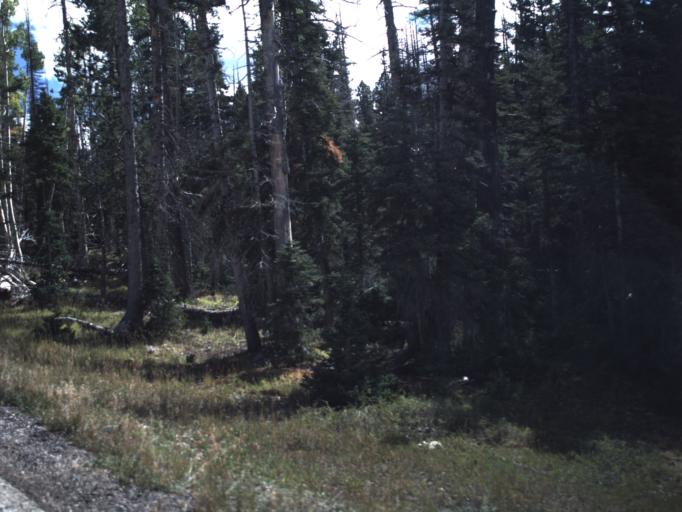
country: US
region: Utah
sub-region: Iron County
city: Parowan
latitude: 37.5317
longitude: -112.7672
